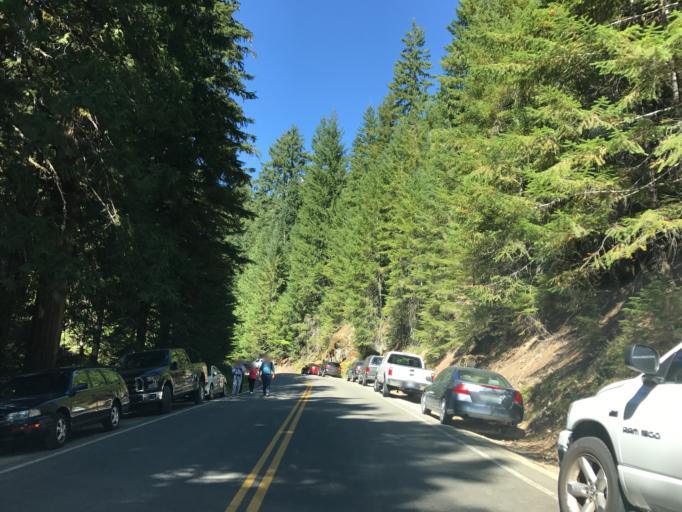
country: US
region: Washington
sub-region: Pierce County
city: Buckley
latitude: 46.7591
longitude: -121.5580
